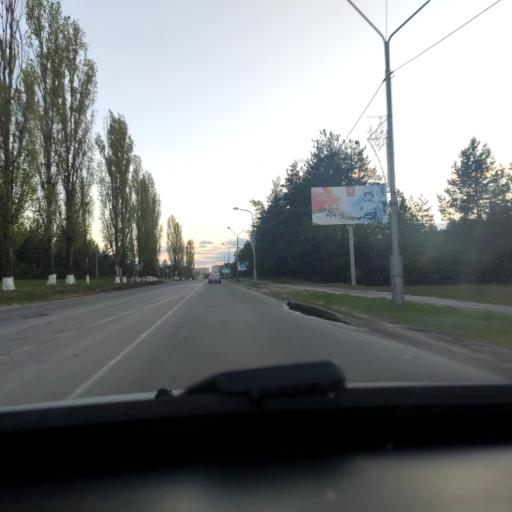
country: RU
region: Voronezj
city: Novovoronezh
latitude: 51.3256
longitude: 39.2397
